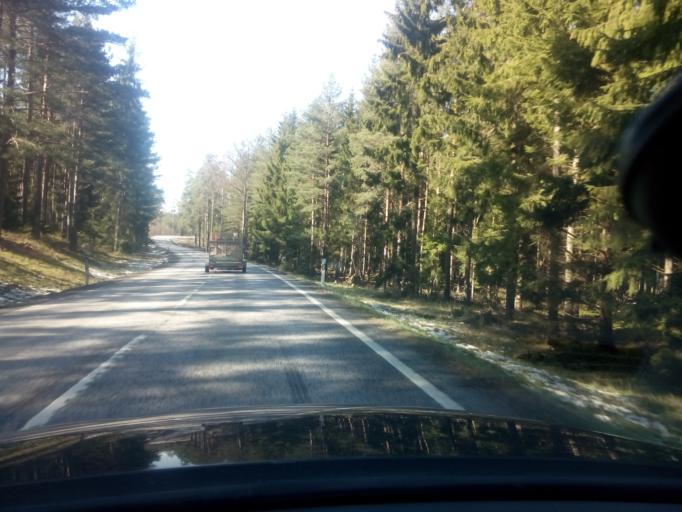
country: SE
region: Soedermanland
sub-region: Nykopings Kommun
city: Stigtomta
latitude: 58.8951
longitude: 16.8286
